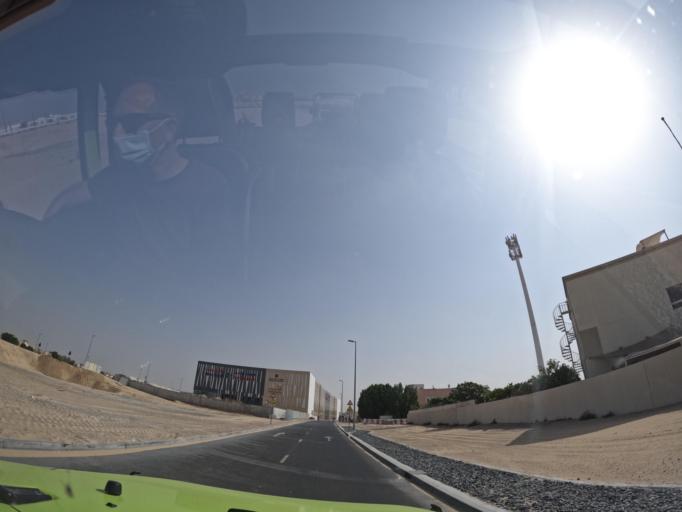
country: AE
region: Ash Shariqah
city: Sharjah
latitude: 25.2069
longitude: 55.4235
